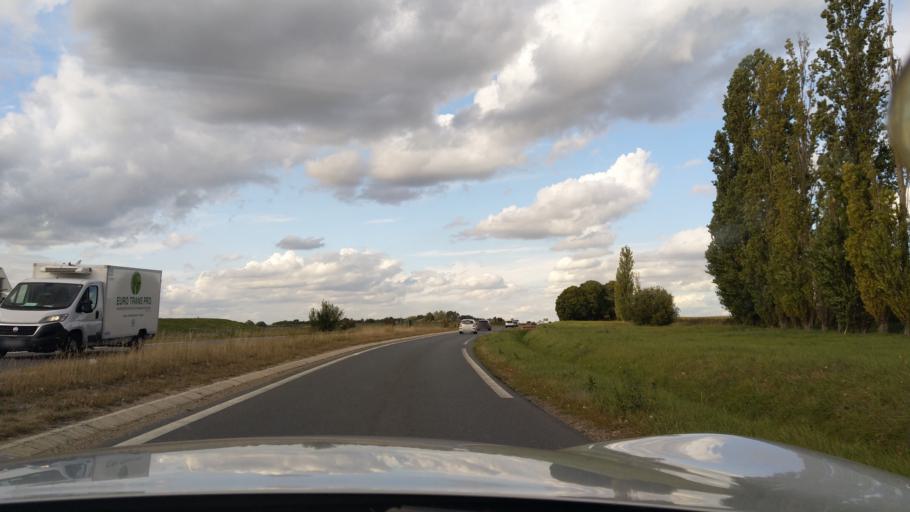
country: FR
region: Ile-de-France
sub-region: Departement de Seine-et-Marne
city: Moussy-le-Neuf
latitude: 49.0198
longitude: 2.5833
